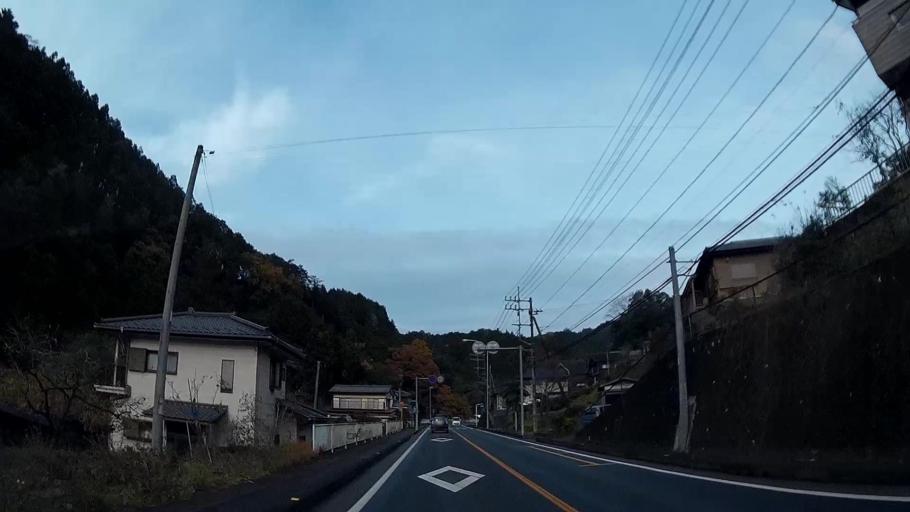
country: JP
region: Saitama
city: Morohongo
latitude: 35.9163
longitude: 139.2158
